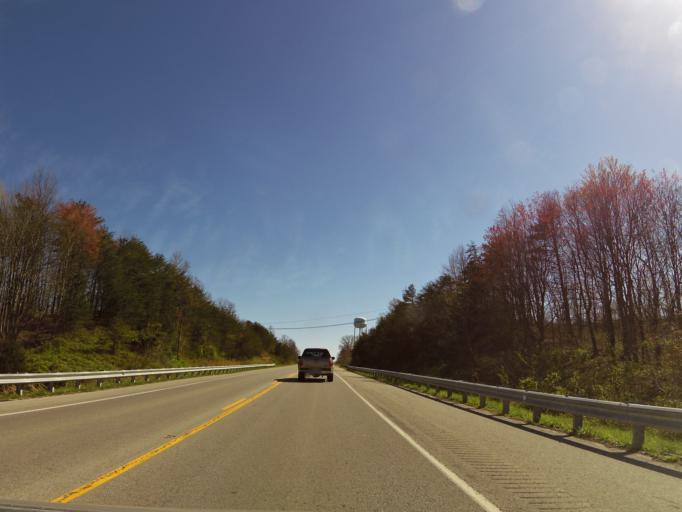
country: US
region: Kentucky
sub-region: McCreary County
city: Pine Knot
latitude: 36.6359
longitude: -84.4347
